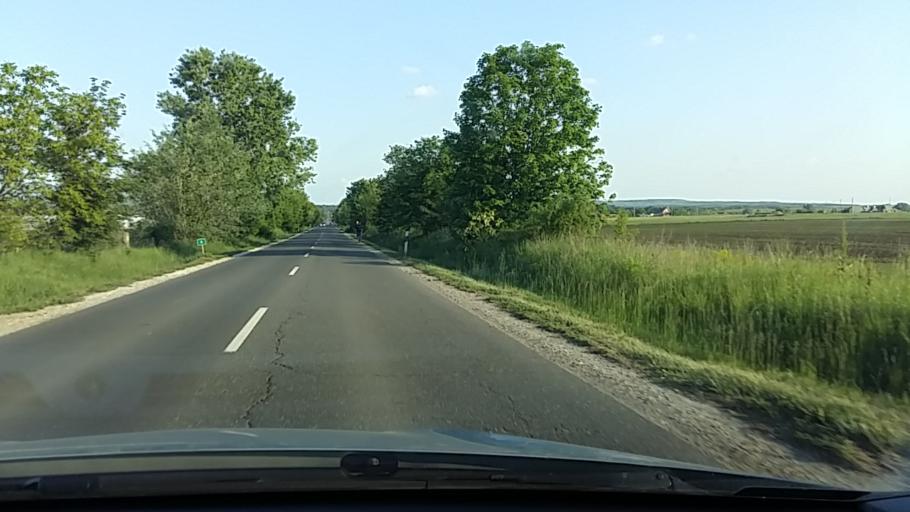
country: HU
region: Pest
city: Szod
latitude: 47.7271
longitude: 19.2263
